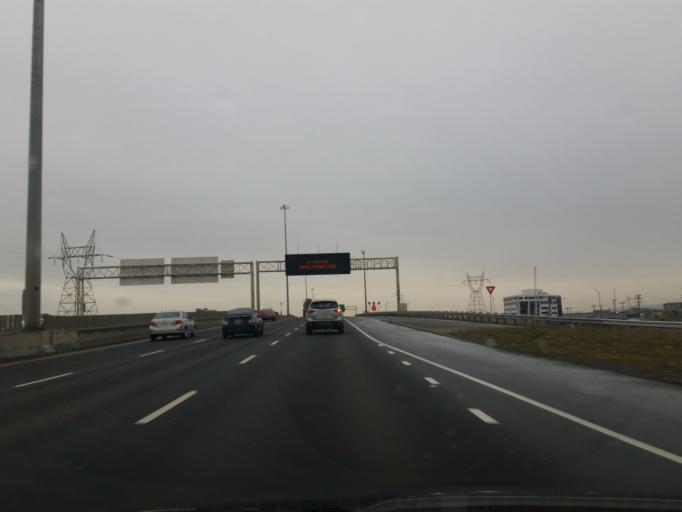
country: CA
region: Quebec
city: Quebec
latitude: 46.8323
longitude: -71.2758
